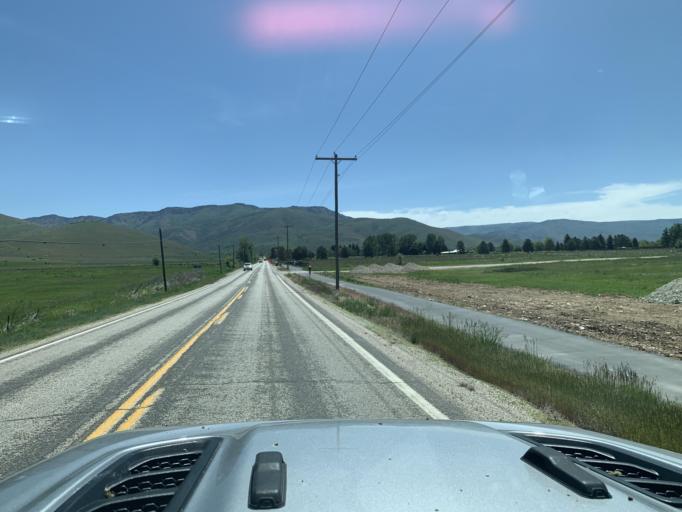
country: US
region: Utah
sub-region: Weber County
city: Wolf Creek
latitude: 41.2932
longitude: -111.7865
